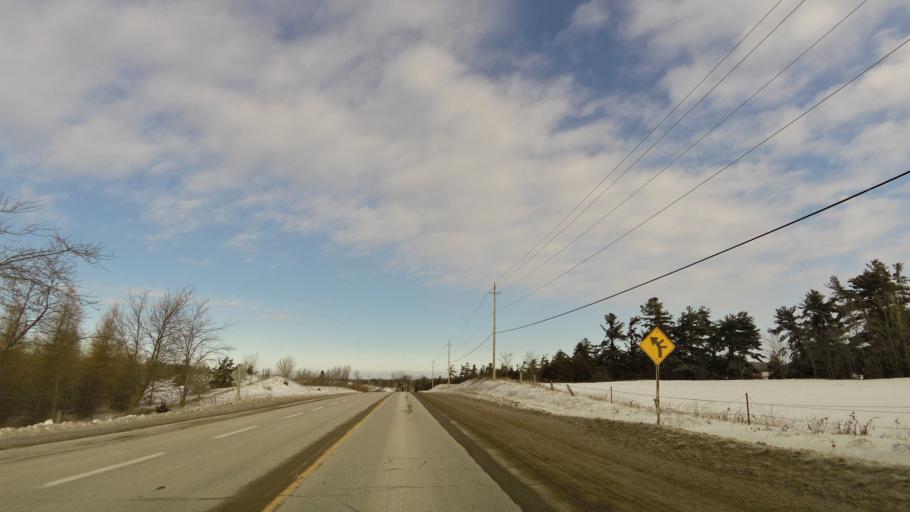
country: CA
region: Ontario
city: Quinte West
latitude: 44.0992
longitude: -77.7679
